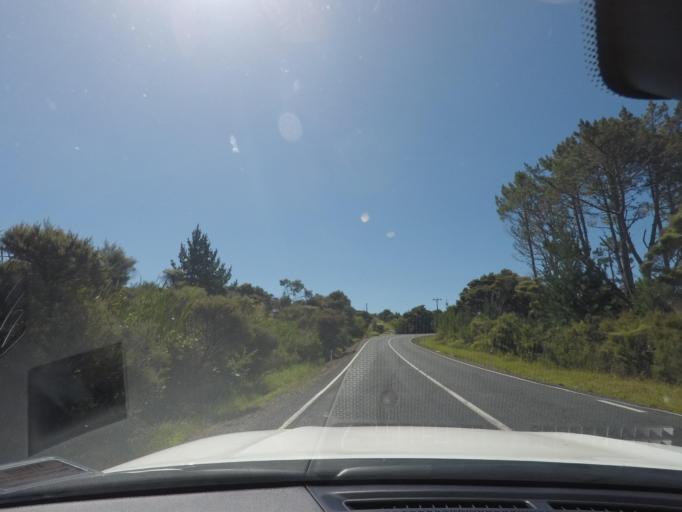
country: NZ
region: Auckland
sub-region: Auckland
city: Parakai
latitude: -36.5842
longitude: 174.3307
